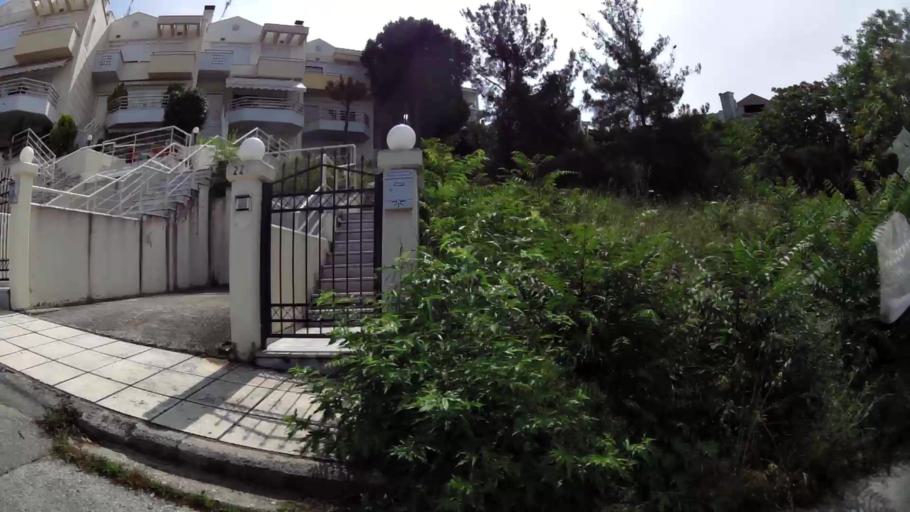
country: GR
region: Central Macedonia
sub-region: Nomos Thessalonikis
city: Panorama
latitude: 40.5802
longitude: 23.0207
